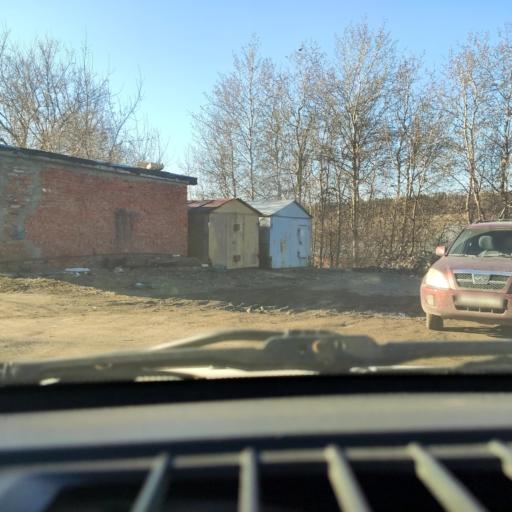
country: RU
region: Perm
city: Perm
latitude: 58.0692
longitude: 56.3625
